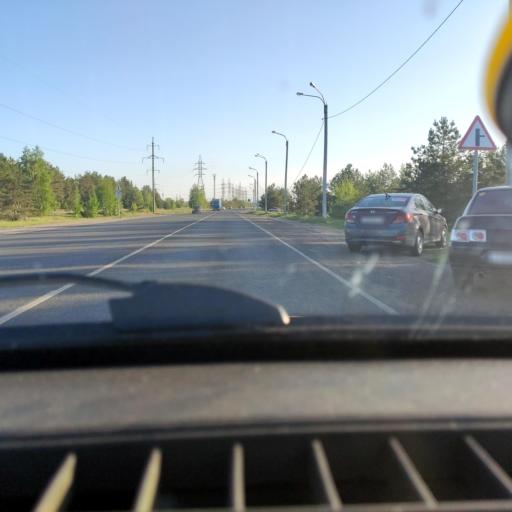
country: RU
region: Samara
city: Zhigulevsk
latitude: 53.5662
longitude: 49.5471
